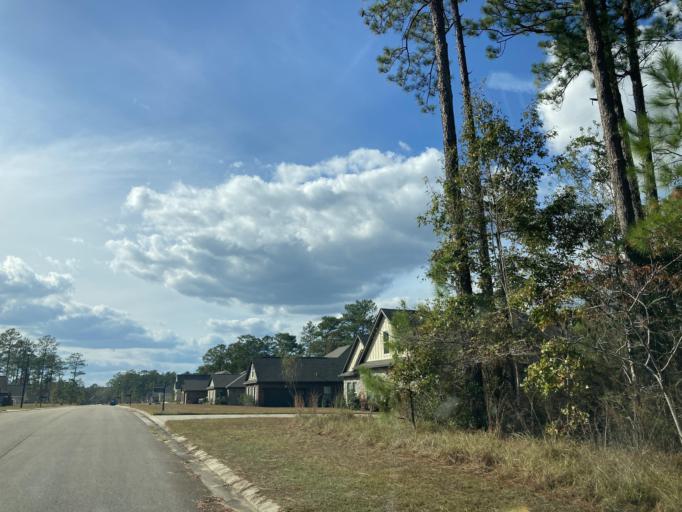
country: US
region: Mississippi
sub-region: Lamar County
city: Arnold Line
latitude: 31.3461
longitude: -89.3672
